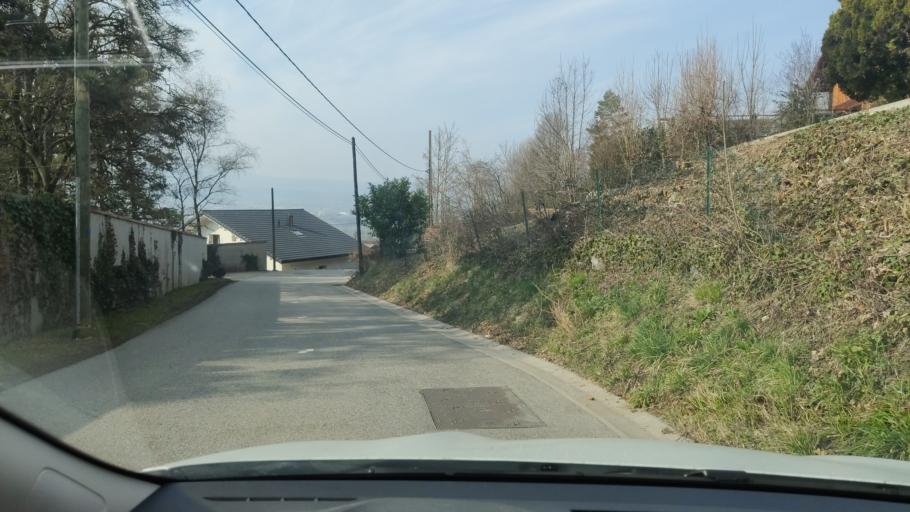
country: FR
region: Rhone-Alpes
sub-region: Departement de la Haute-Savoie
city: Bonneville
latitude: 46.0881
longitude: 6.4149
